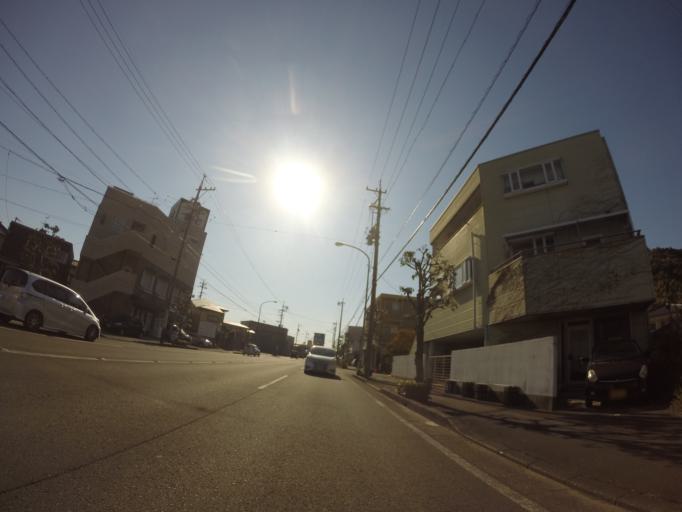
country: JP
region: Shizuoka
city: Shizuoka-shi
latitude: 34.9972
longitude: 138.3796
